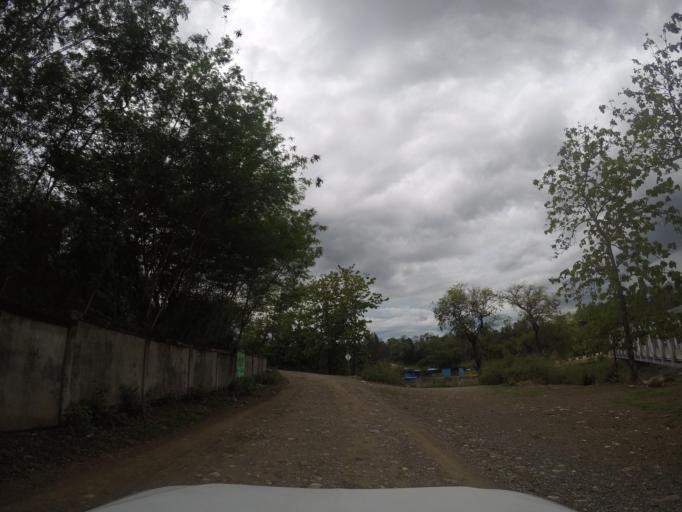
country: TL
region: Bobonaro
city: Maliana
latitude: -8.9731
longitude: 125.2232
